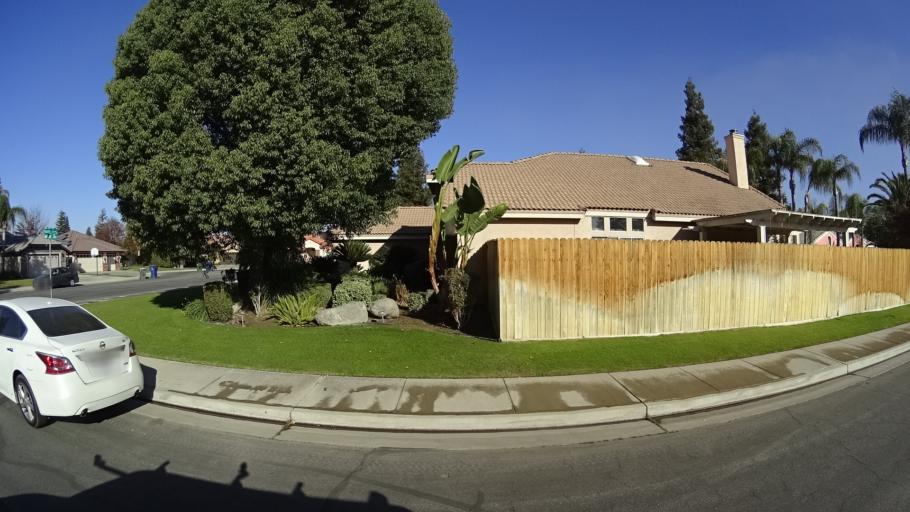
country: US
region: California
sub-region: Kern County
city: Greenfield
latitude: 35.2768
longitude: -119.0403
